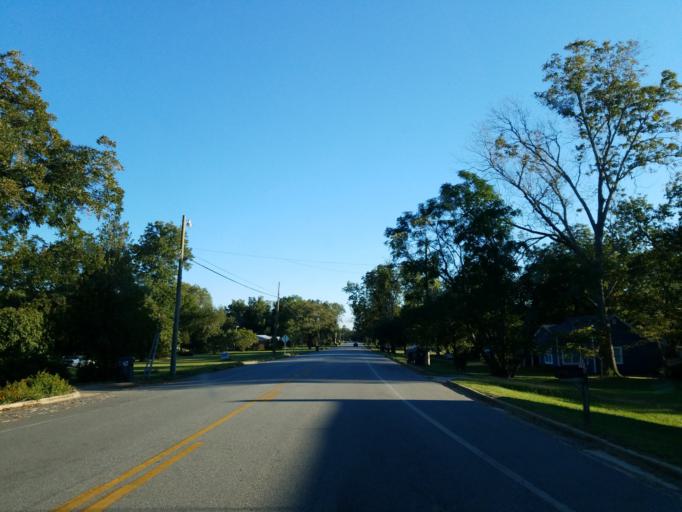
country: US
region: Georgia
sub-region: Worth County
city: Sylvester
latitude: 31.7024
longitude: -83.8858
